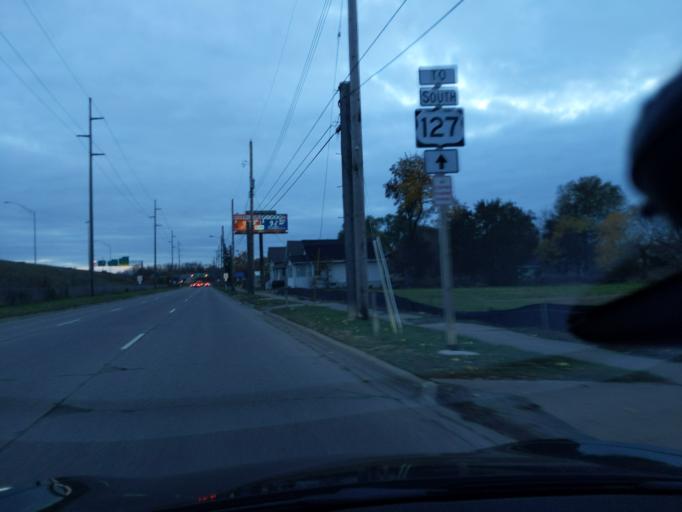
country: US
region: Michigan
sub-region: Ingham County
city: East Lansing
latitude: 42.7330
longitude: -84.5112
